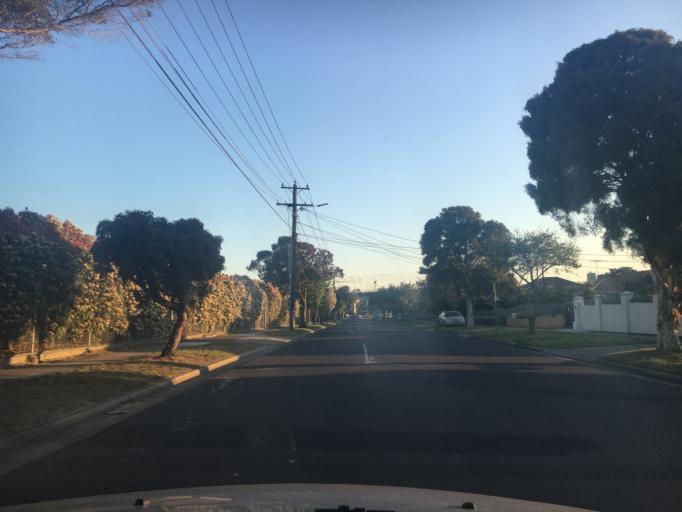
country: AU
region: Victoria
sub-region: Monash
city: Clayton
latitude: -37.9264
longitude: 145.1264
